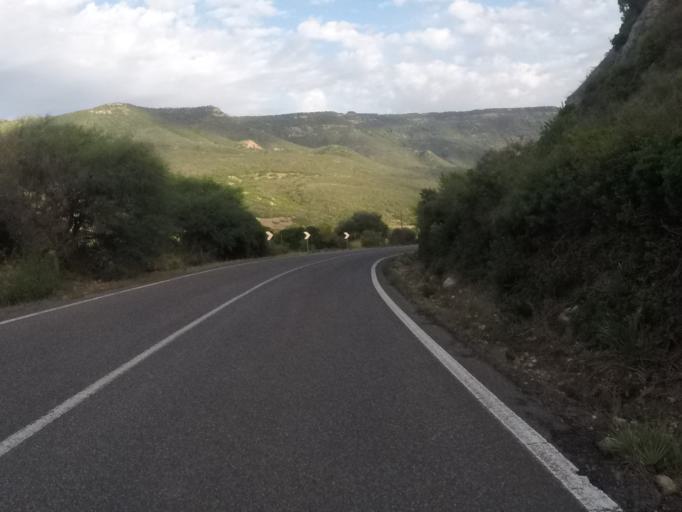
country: IT
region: Sardinia
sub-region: Provincia di Sassari
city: Alghero
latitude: 40.5015
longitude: 8.3643
